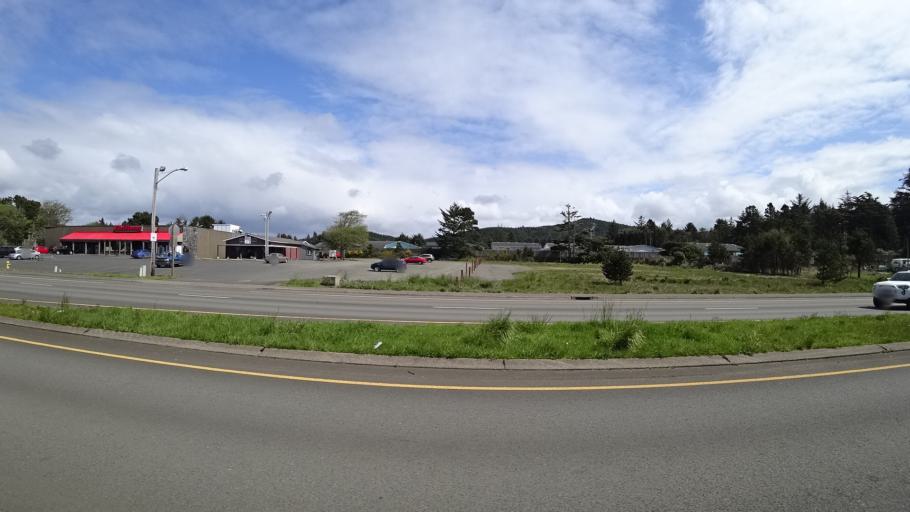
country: US
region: Oregon
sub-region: Lincoln County
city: Lincoln Beach
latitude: 44.8496
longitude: -124.0446
